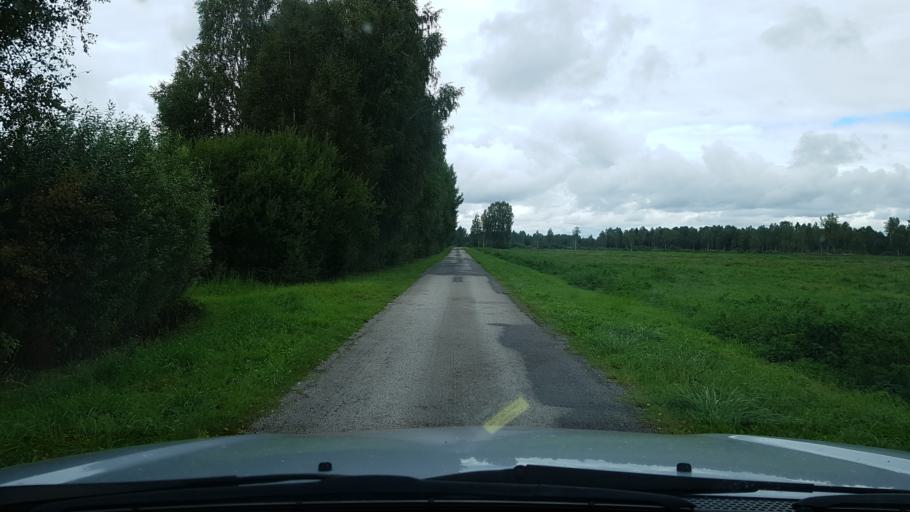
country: EE
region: Harju
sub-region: Raasiku vald
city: Arukula
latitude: 59.2986
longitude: 25.0572
